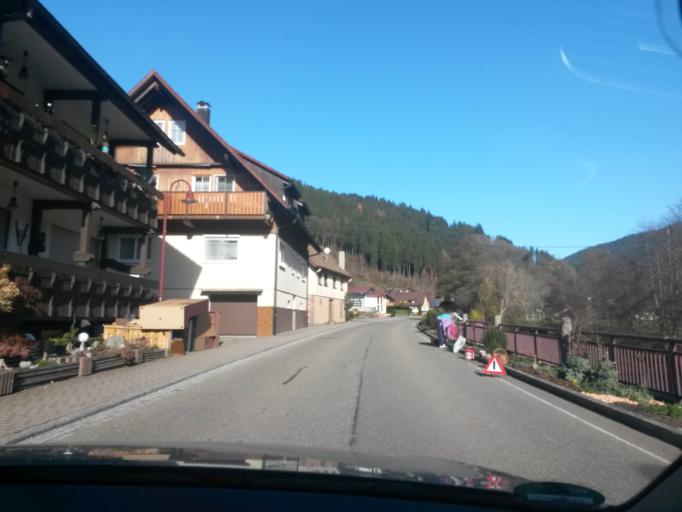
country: DE
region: Baden-Wuerttemberg
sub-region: Karlsruhe Region
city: Bad Rippoldsau-Schapbach
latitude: 48.3815
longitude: 8.2979
